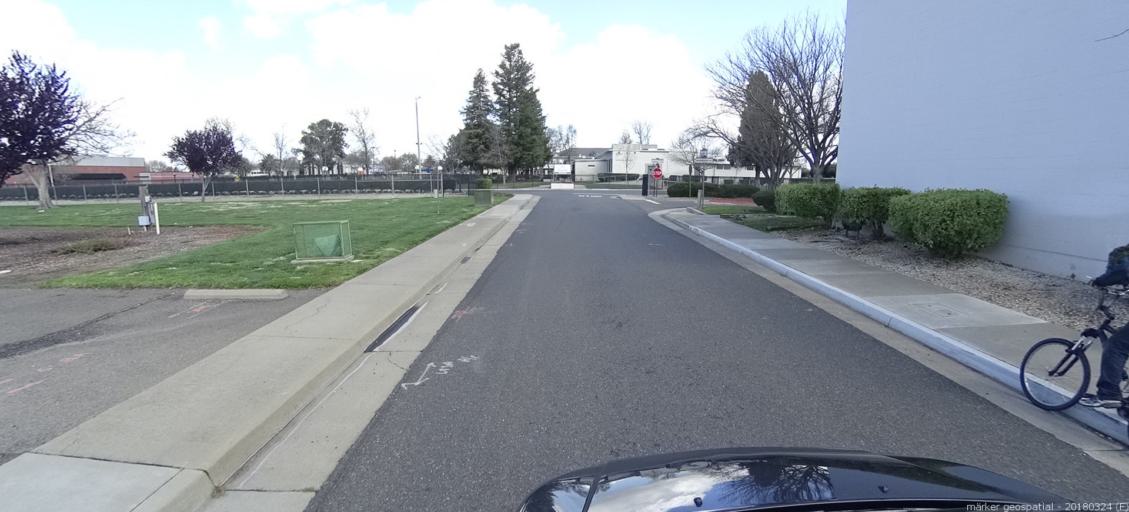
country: US
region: California
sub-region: Sacramento County
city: North Highlands
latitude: 38.6680
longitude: -121.3853
